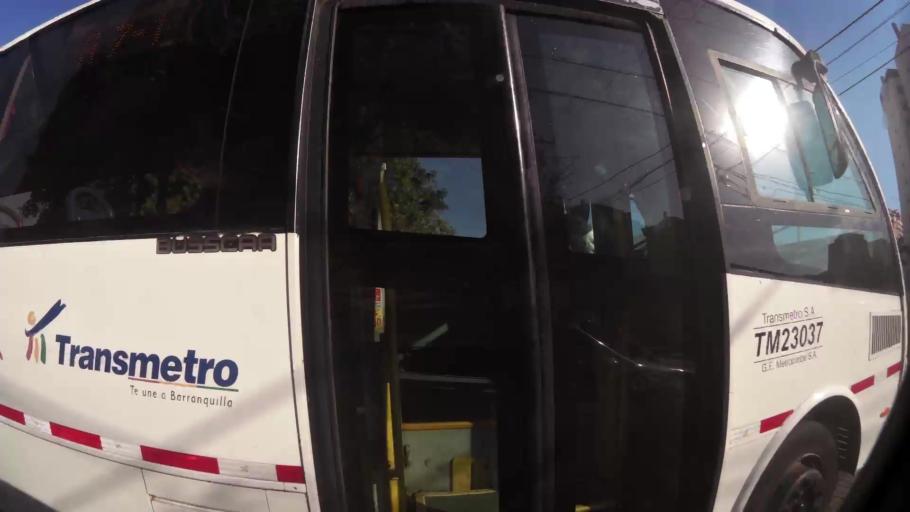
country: CO
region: Atlantico
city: Barranquilla
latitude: 11.0014
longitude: -74.8360
